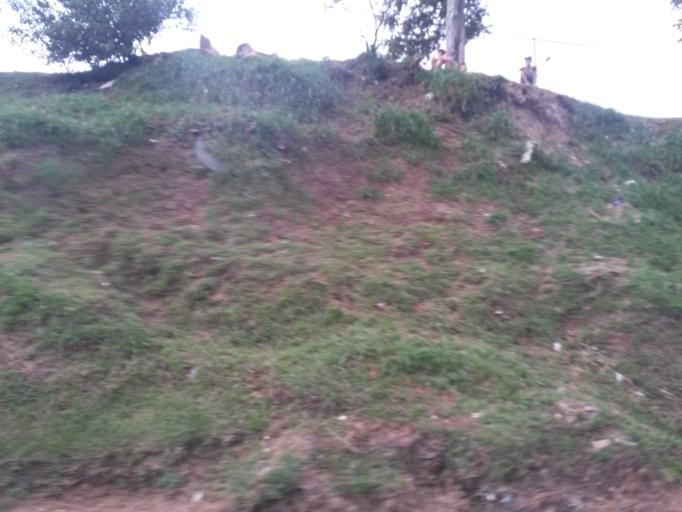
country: CO
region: Cauca
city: Popayan
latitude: 2.4420
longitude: -76.6266
